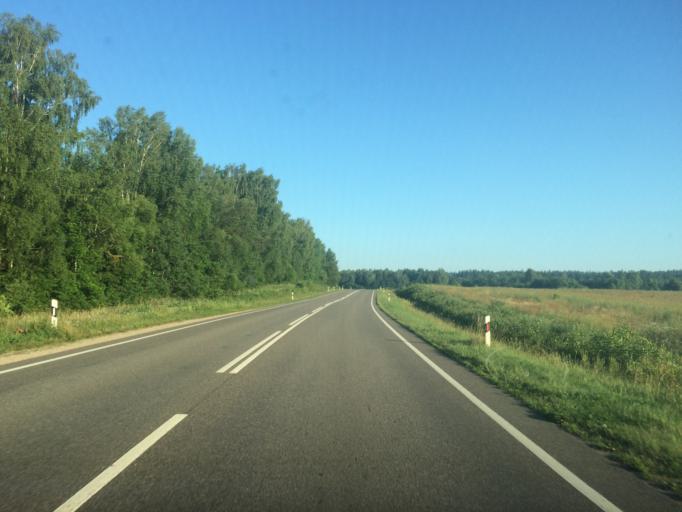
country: LT
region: Utenos apskritis
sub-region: Anyksciai
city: Anyksciai
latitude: 55.4010
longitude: 25.1394
